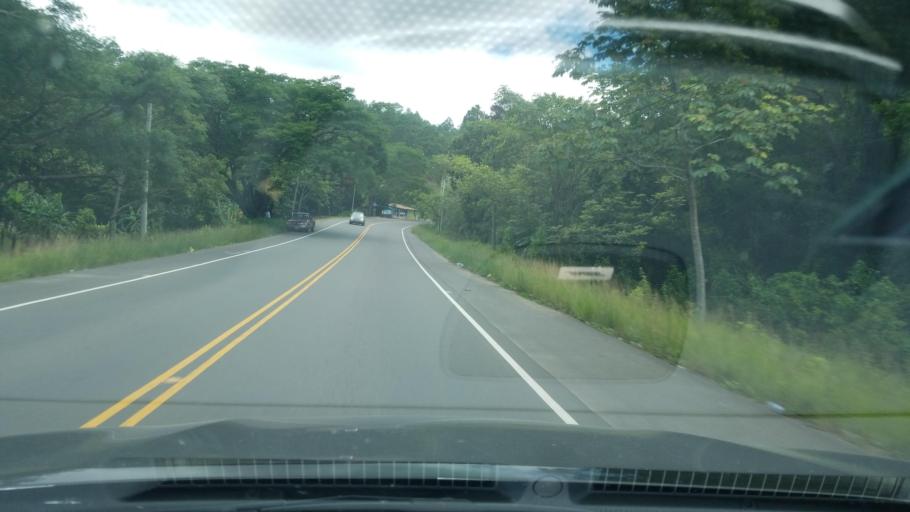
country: HN
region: Francisco Morazan
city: Talanga
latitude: 14.3669
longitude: -87.1394
